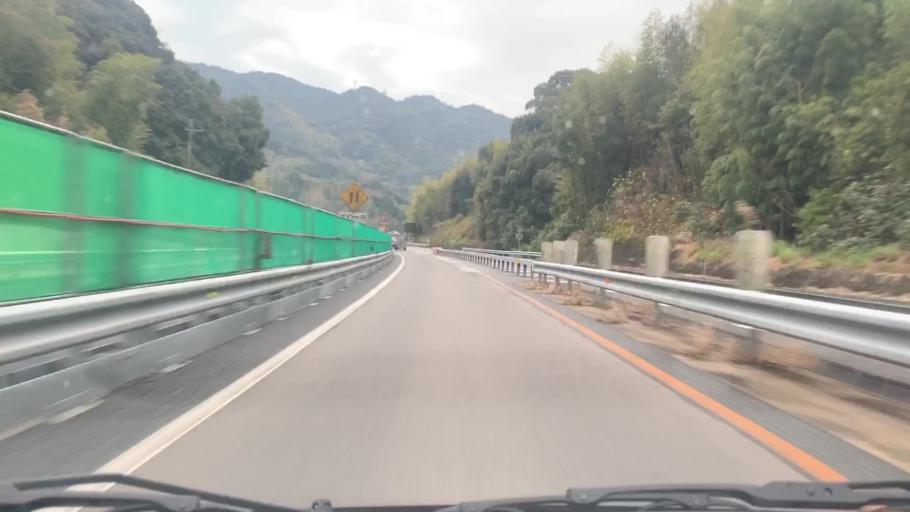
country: JP
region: Nagasaki
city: Obita
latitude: 32.8035
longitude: 129.9659
